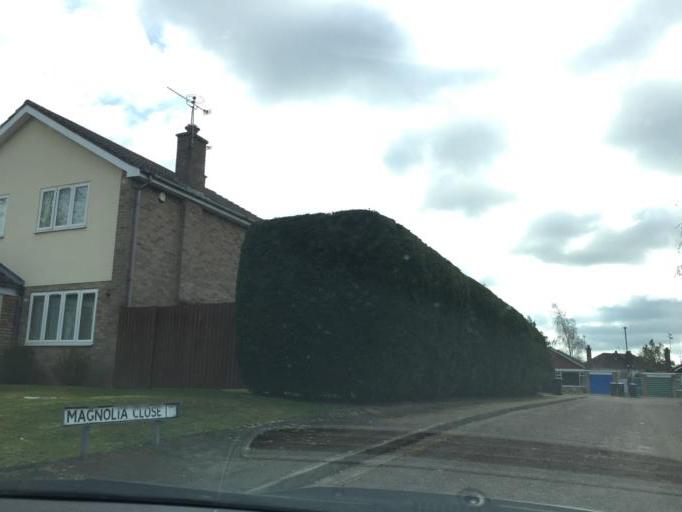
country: GB
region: England
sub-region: Coventry
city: Coventry
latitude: 52.3846
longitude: -1.5178
